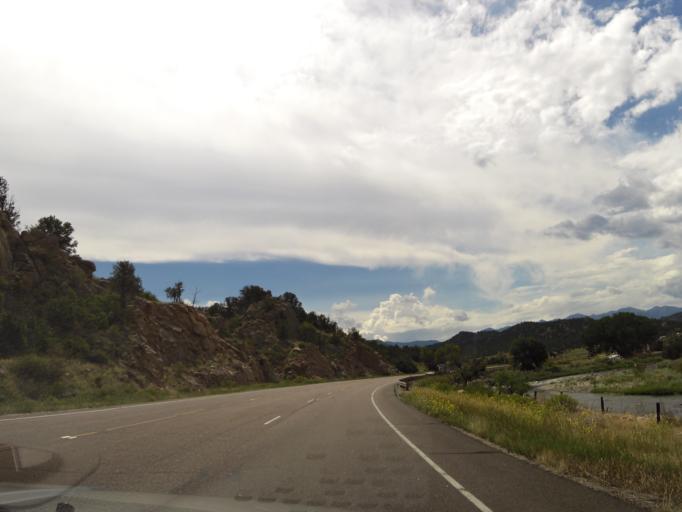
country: US
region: Colorado
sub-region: Custer County
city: Westcliffe
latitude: 38.3936
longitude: -105.6208
